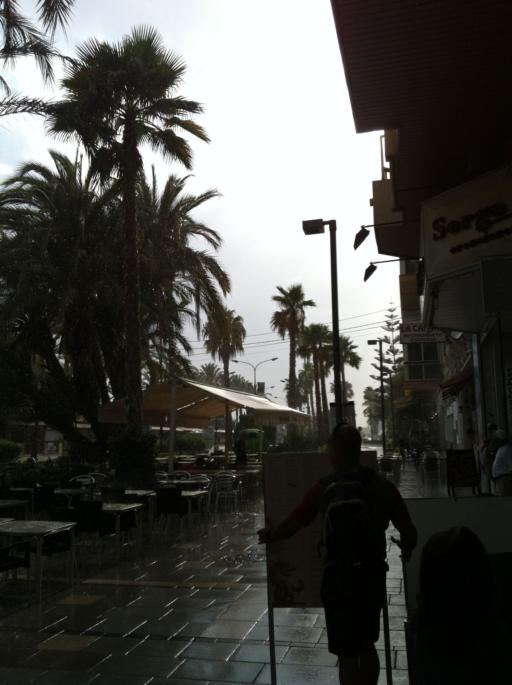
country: ES
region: Valencia
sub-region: Provincia de Alicante
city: Torrevieja
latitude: 37.9757
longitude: -0.6793
